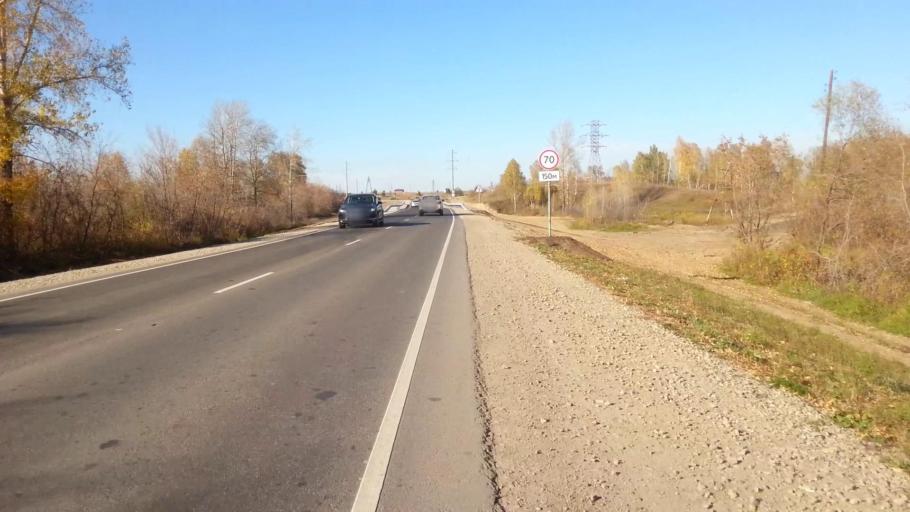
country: RU
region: Altai Krai
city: Sannikovo
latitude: 53.3259
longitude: 83.9421
